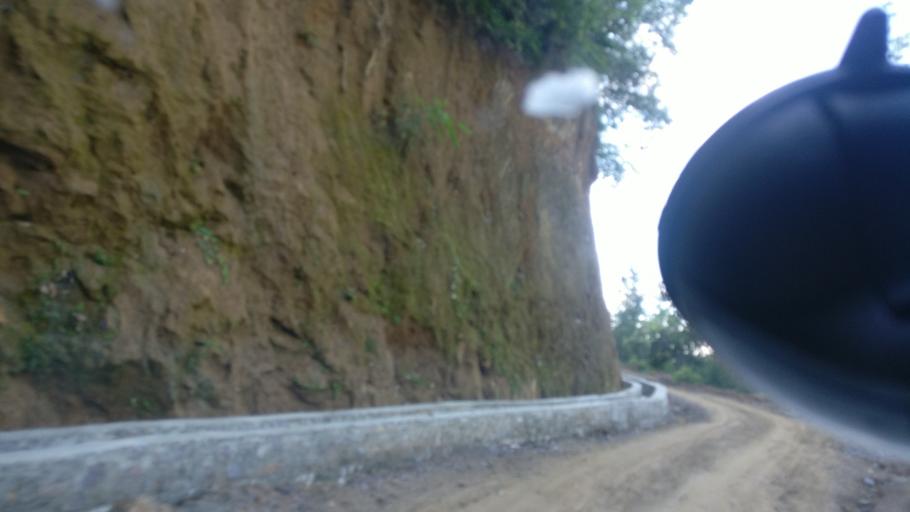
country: NP
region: Western Region
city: Baglung
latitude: 28.1568
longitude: 83.6540
